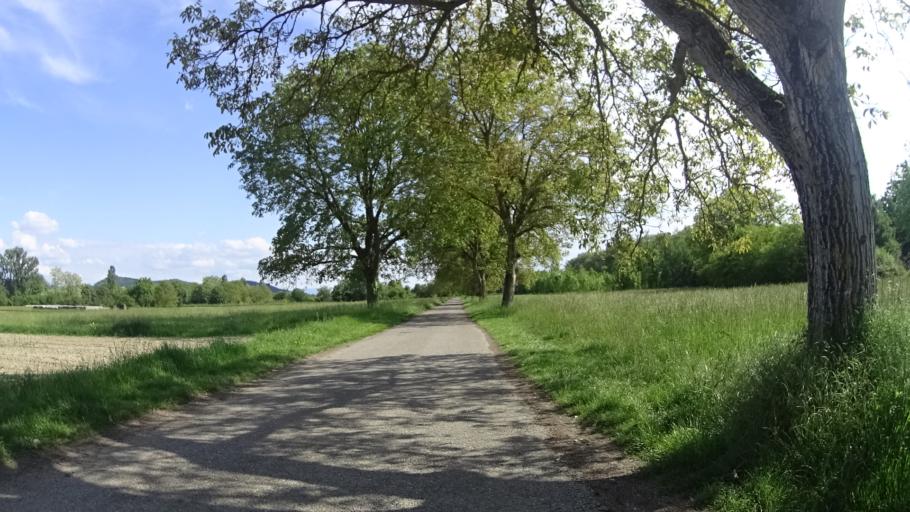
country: DE
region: Baden-Wuerttemberg
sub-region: Freiburg Region
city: Vogtsburg
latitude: 48.0933
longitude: 7.5937
